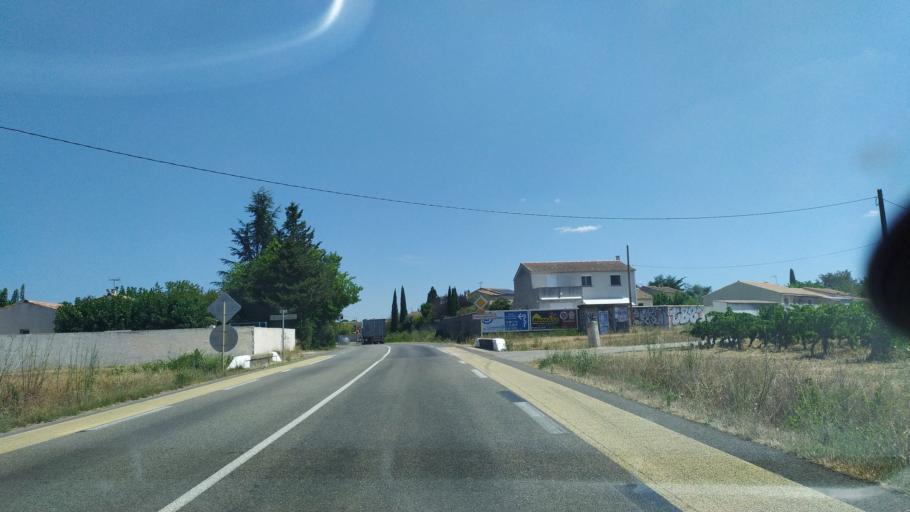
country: FR
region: Languedoc-Roussillon
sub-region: Departement du Gard
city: Caissargues
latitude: 43.7919
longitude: 4.3781
